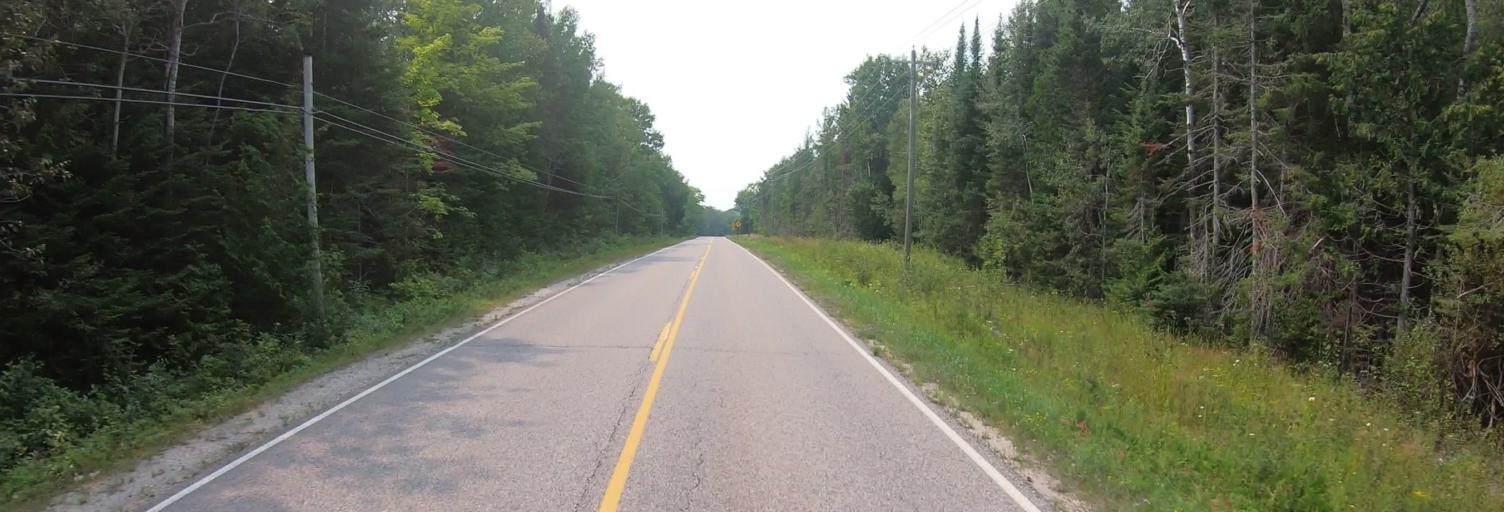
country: CA
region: Ontario
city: Thessalon
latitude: 45.9998
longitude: -83.9734
